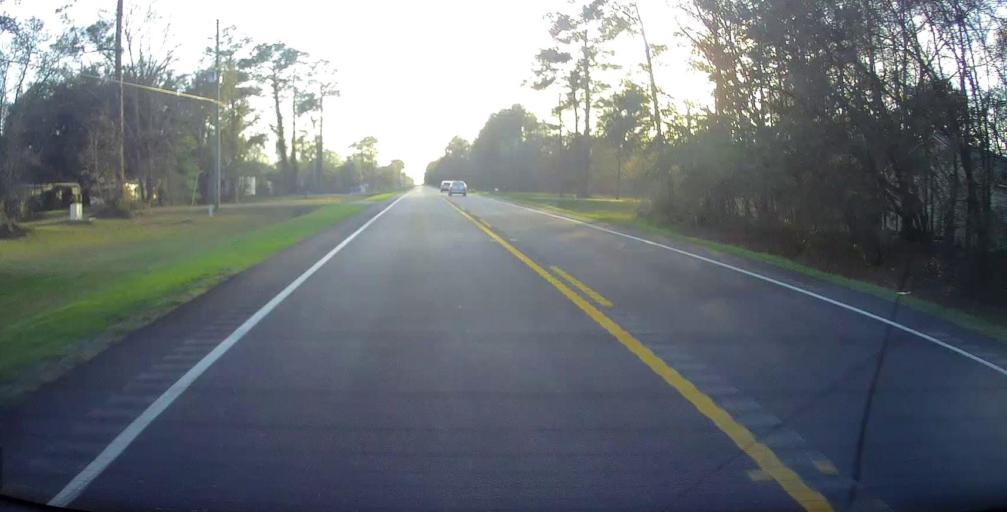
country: US
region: Georgia
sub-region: Bryan County
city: Pembroke
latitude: 32.1535
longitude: -81.5105
